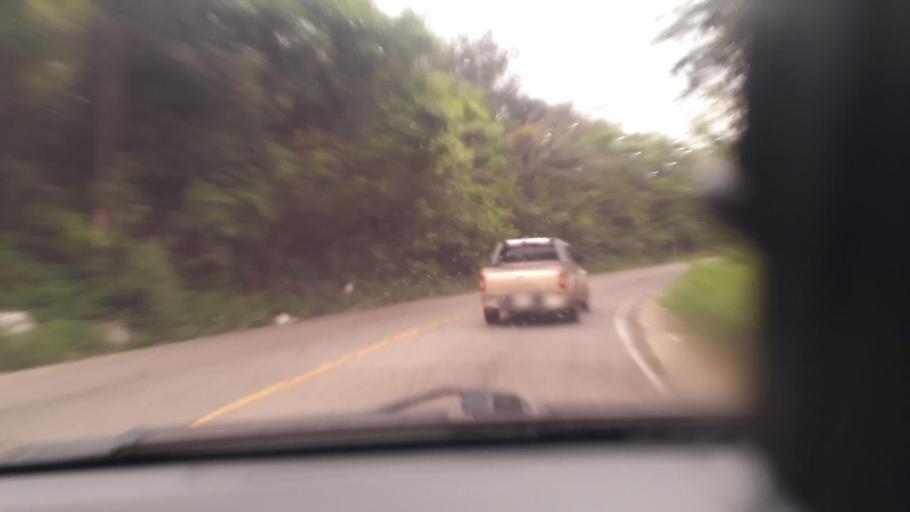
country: GT
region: Jutiapa
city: Jalpatagua
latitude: 14.1837
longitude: -90.0437
